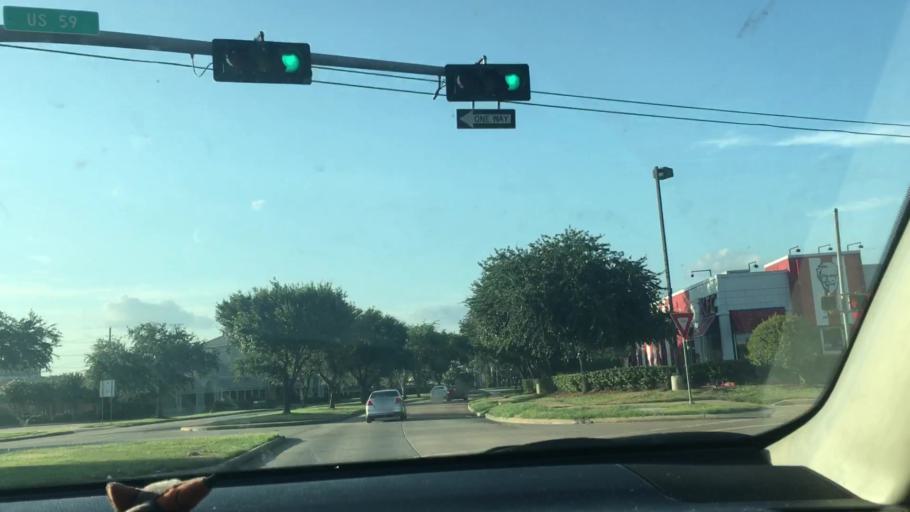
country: US
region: Texas
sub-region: Fort Bend County
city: Meadows Place
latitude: 29.6397
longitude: -95.5816
